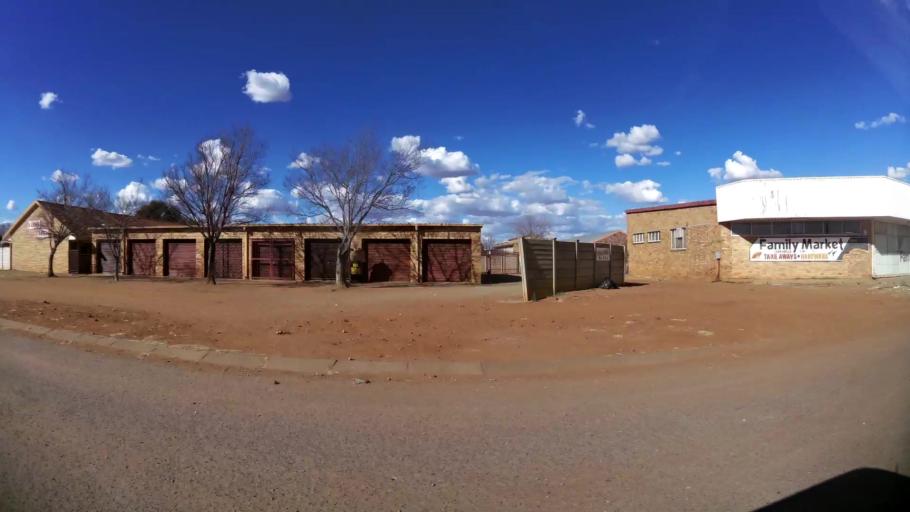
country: ZA
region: North-West
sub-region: Dr Kenneth Kaunda District Municipality
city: Klerksdorp
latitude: -26.8248
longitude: 26.6585
